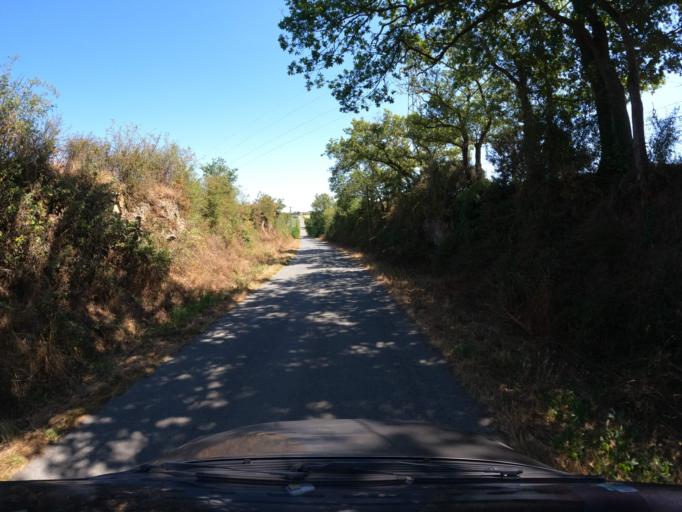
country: FR
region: Pays de la Loire
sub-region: Departement de Maine-et-Loire
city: Saint-Christophe-du-Bois
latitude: 47.0391
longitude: -0.9532
